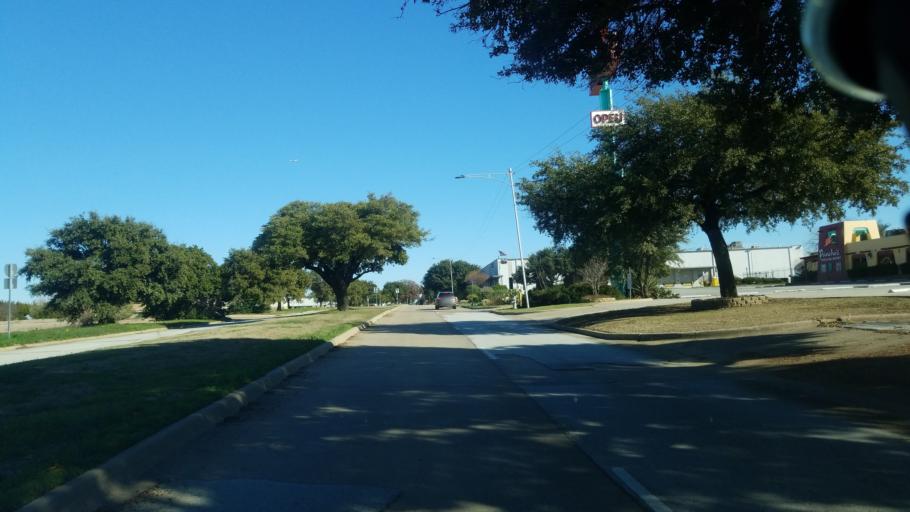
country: US
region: Texas
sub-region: Tarrant County
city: Arlington
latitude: 32.7565
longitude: -97.0612
